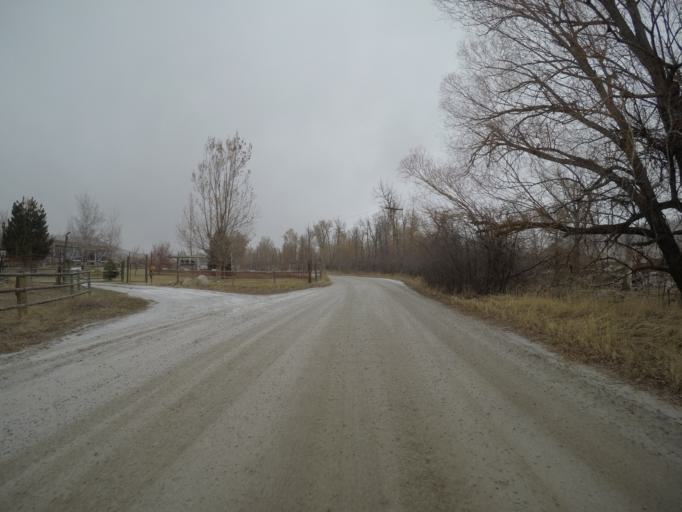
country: US
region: Montana
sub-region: Stillwater County
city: Absarokee
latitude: 45.5266
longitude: -109.4388
